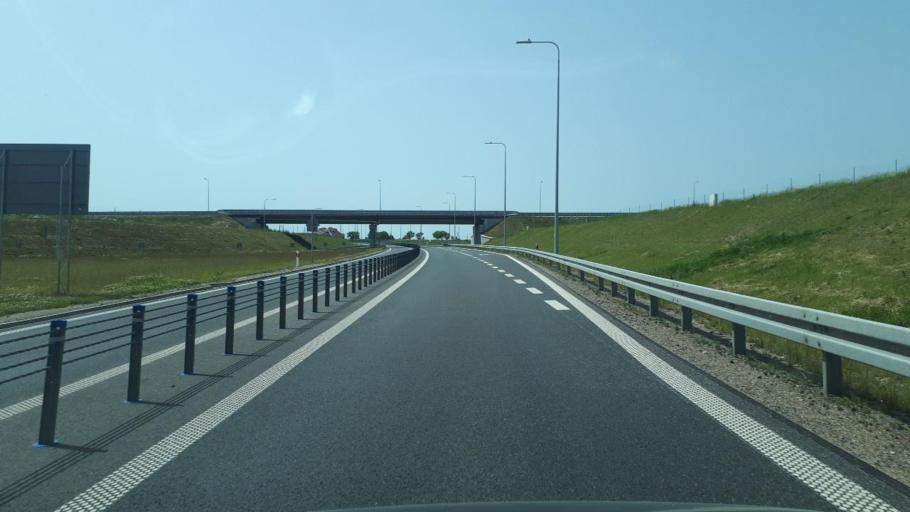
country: PL
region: Greater Poland Voivodeship
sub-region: Powiat kepinski
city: Baranow
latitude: 51.2578
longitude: 18.0161
